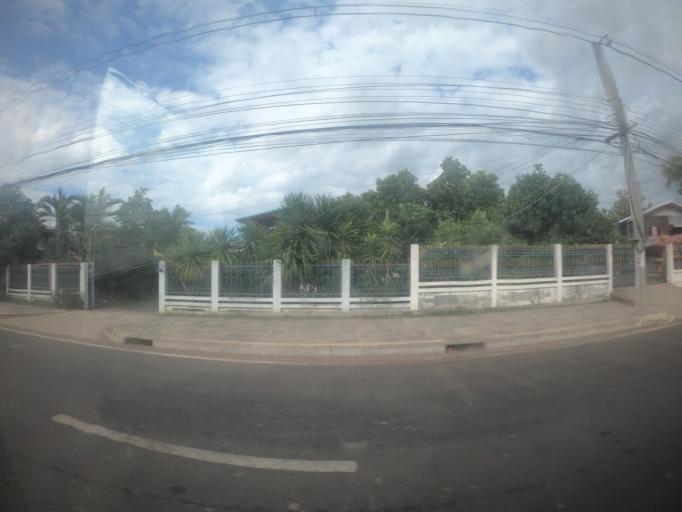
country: TH
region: Surin
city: Prasat
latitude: 14.6262
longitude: 103.4103
